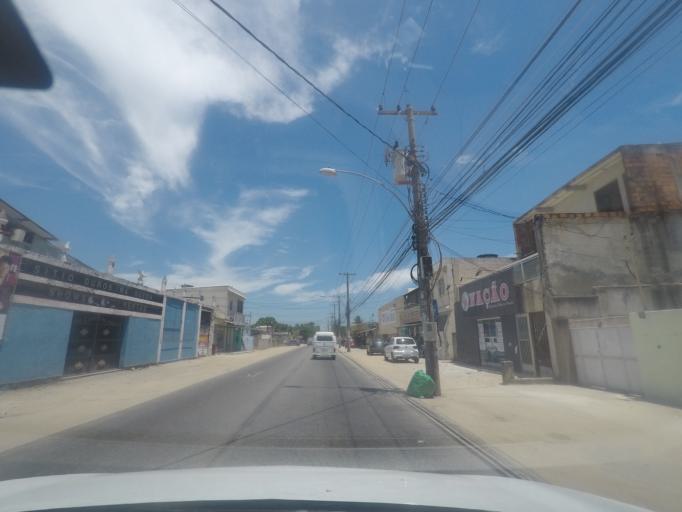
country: BR
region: Rio de Janeiro
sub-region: Itaguai
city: Itaguai
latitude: -22.9406
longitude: -43.6850
